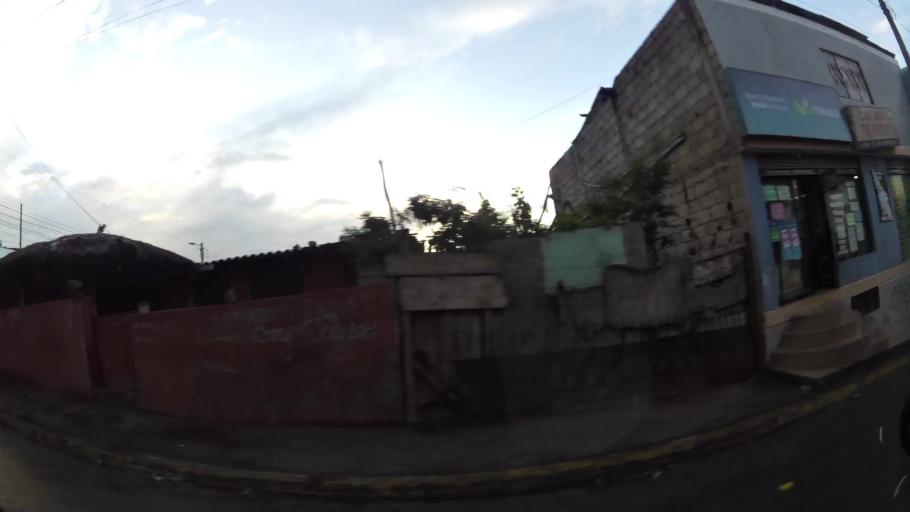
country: EC
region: Pichincha
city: Quito
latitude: -0.0992
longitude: -78.5205
